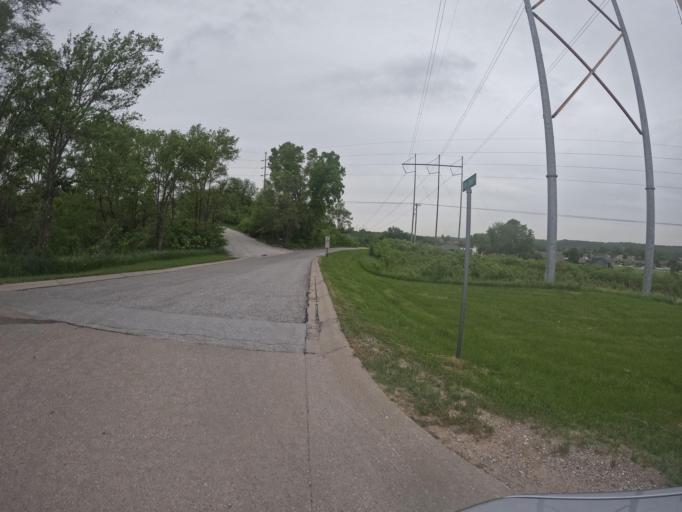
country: US
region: Nebraska
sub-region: Cass County
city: Plattsmouth
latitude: 41.0452
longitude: -95.9584
